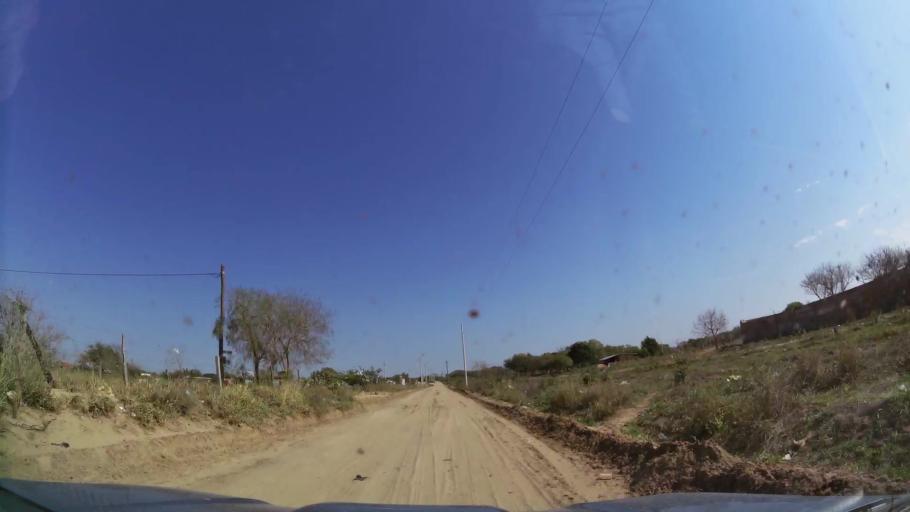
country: BO
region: Santa Cruz
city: Cotoca
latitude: -17.7292
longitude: -63.0716
